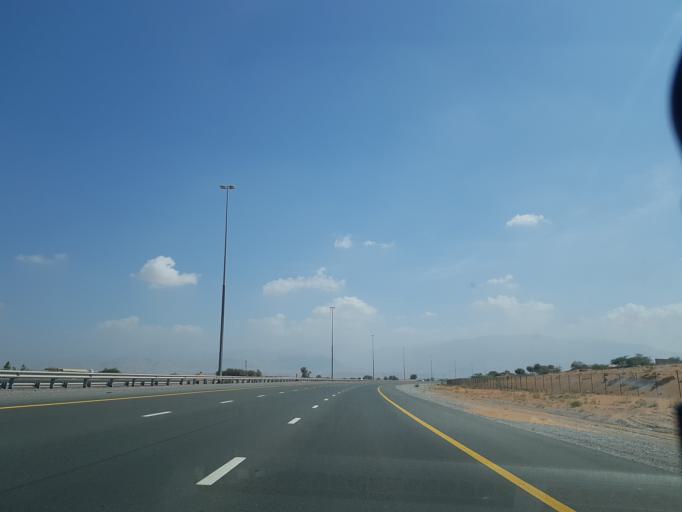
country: AE
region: Ra's al Khaymah
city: Ras al-Khaimah
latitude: 25.7057
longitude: 55.9436
